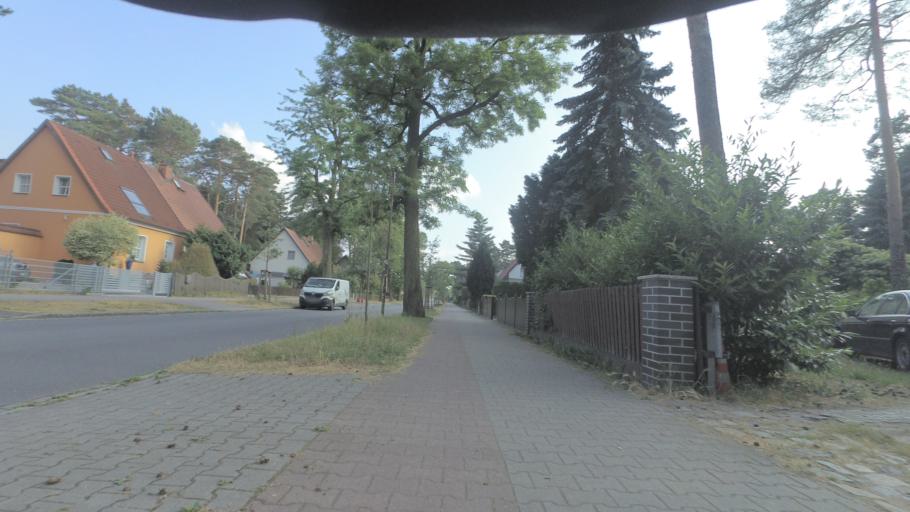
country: DE
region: Brandenburg
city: Rangsdorf
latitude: 52.3359
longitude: 13.4101
